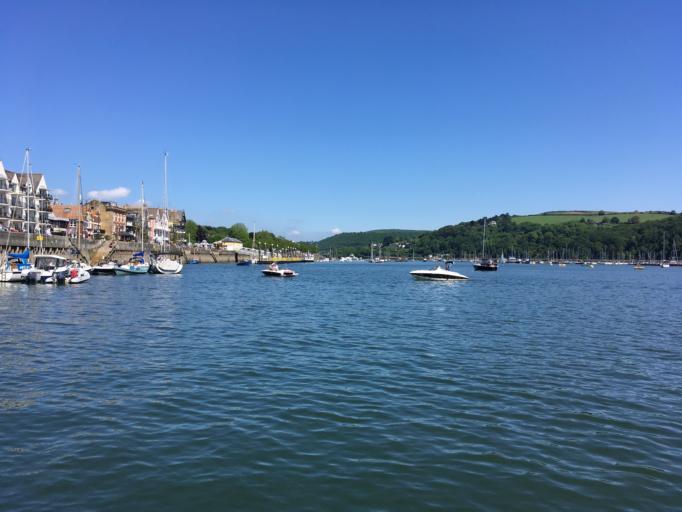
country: GB
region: England
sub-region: Devon
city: Dartmouth
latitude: 50.3488
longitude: -3.5767
